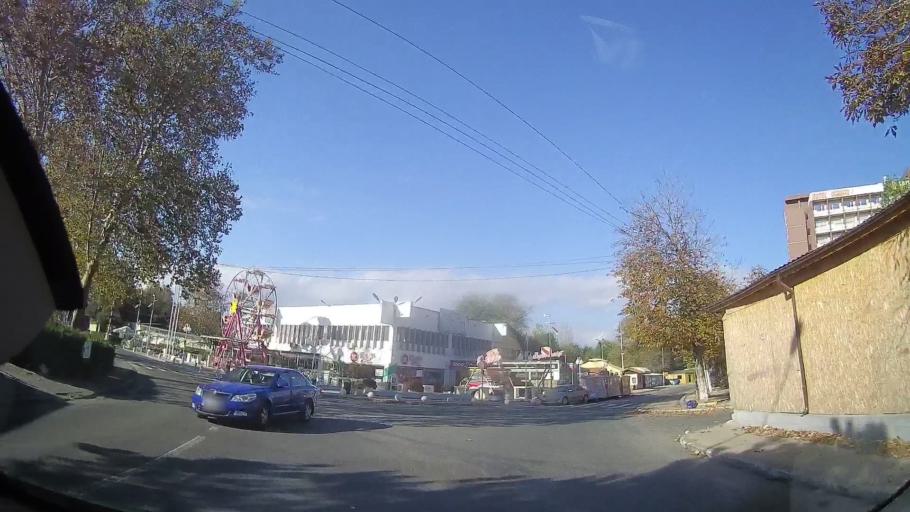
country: RO
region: Constanta
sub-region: Municipiul Mangalia
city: Mangalia
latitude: 43.8561
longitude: 28.6054
